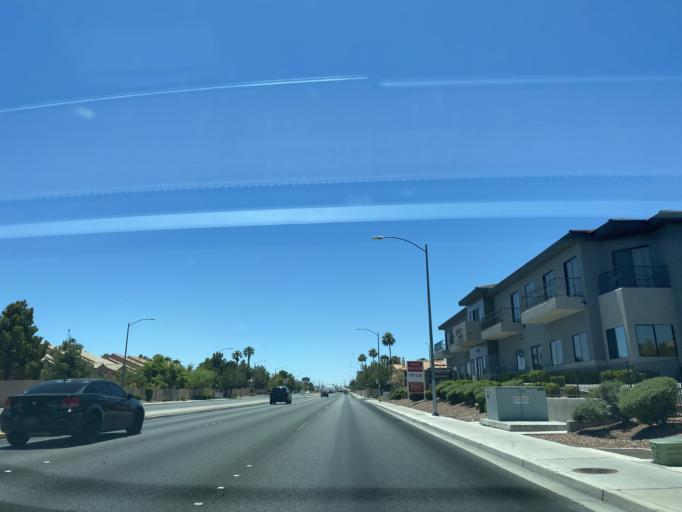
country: US
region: Nevada
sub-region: Clark County
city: Spring Valley
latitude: 36.1861
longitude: -115.2601
